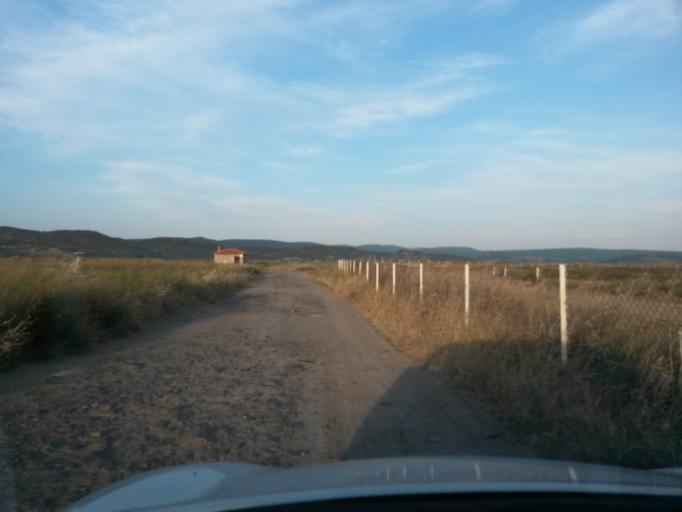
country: GR
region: North Aegean
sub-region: Nomos Lesvou
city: Agia Paraskevi
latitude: 39.2074
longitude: 26.2500
